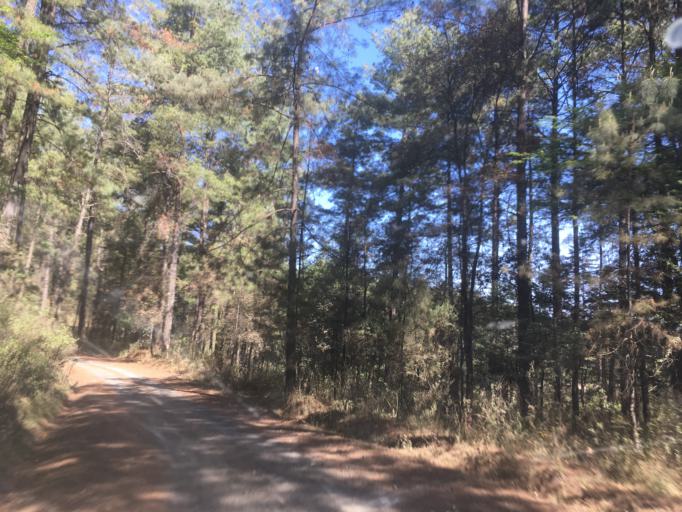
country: MX
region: Michoacan
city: Angahuan
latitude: 19.4905
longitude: -102.2054
